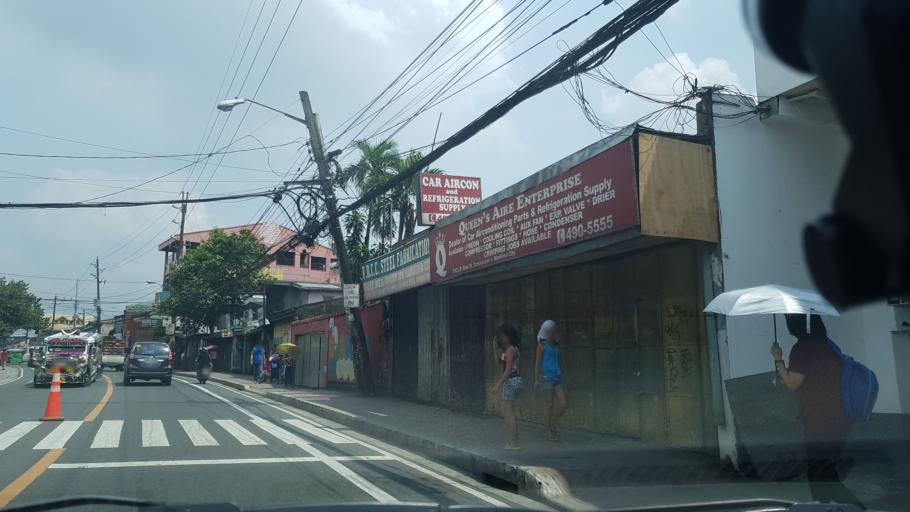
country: PH
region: Metro Manila
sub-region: Marikina
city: Calumpang
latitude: 14.6510
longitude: 121.1029
